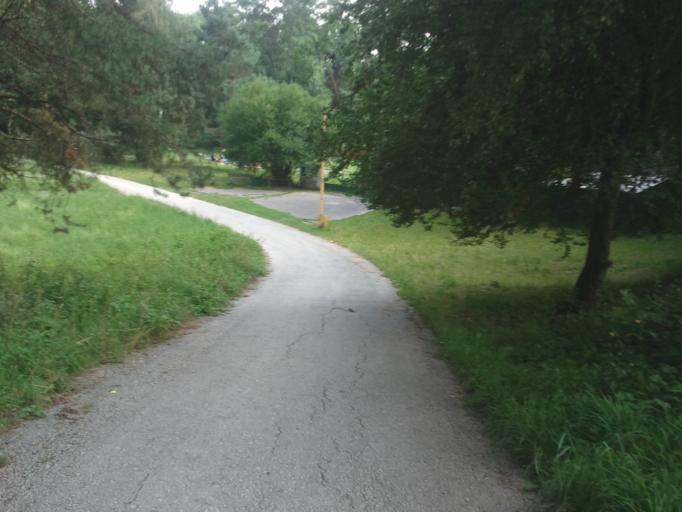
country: SK
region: Nitriansky
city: Bojnice
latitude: 48.7763
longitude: 18.5928
